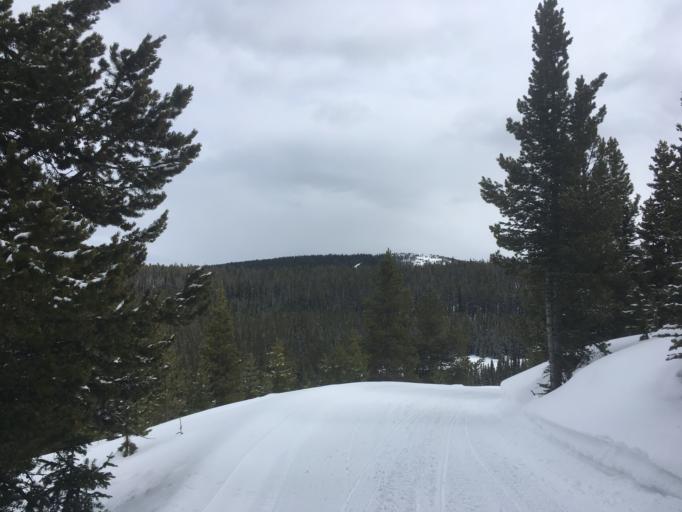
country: US
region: Montana
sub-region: Meagher County
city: White Sulphur Springs
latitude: 46.8458
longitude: -110.7074
